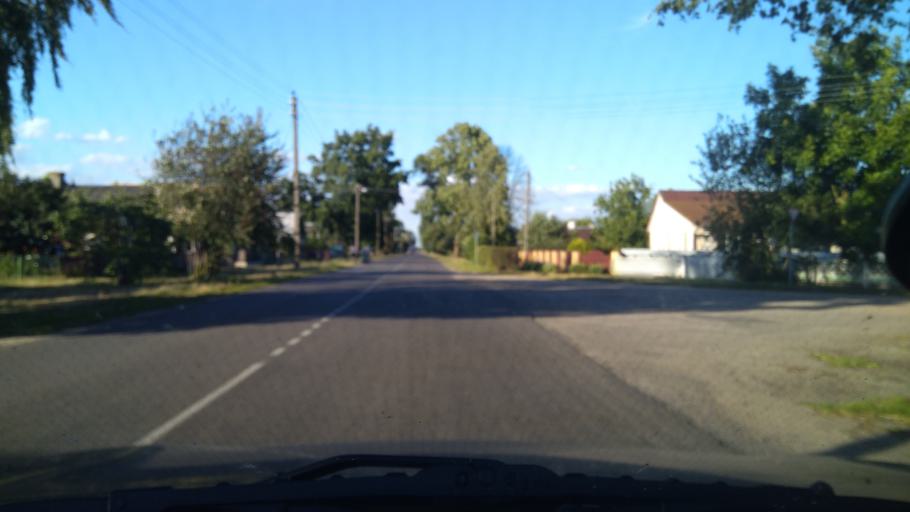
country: BY
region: Brest
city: Byaroza
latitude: 52.5835
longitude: 24.8629
